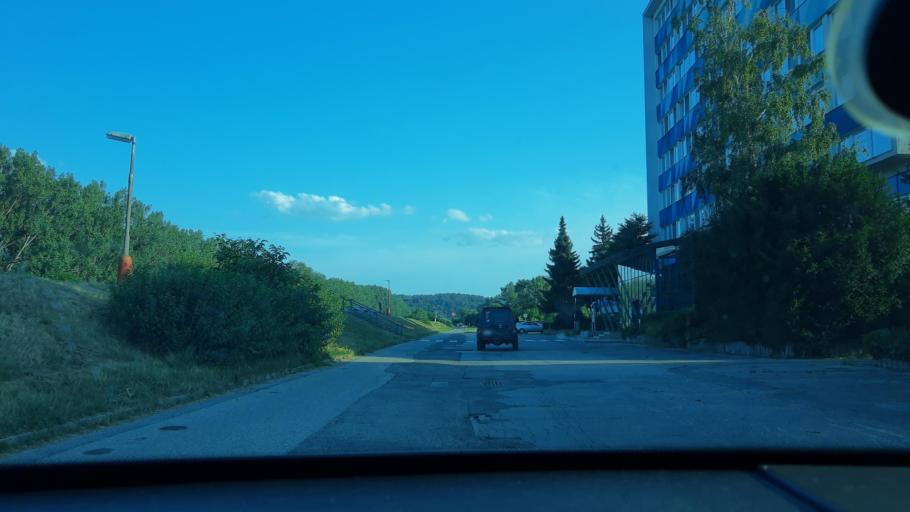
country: SK
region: Trnavsky
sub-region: Okres Trnava
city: Piestany
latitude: 48.6010
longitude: 17.8404
